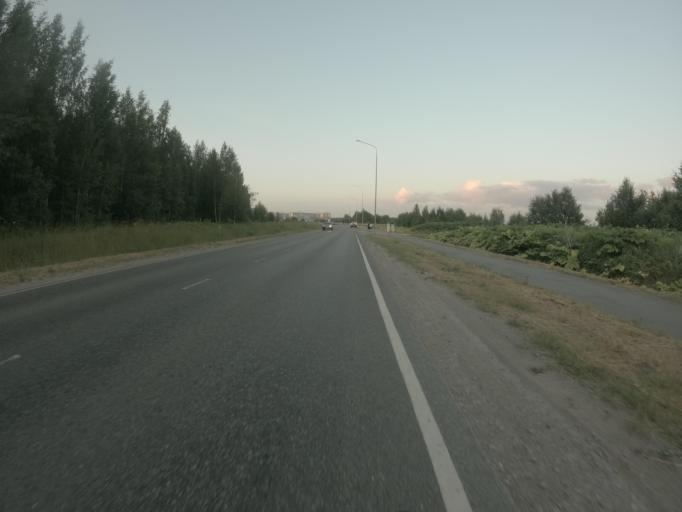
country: RU
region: Leningrad
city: Yanino Vtoroye
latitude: 59.9561
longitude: 30.5835
